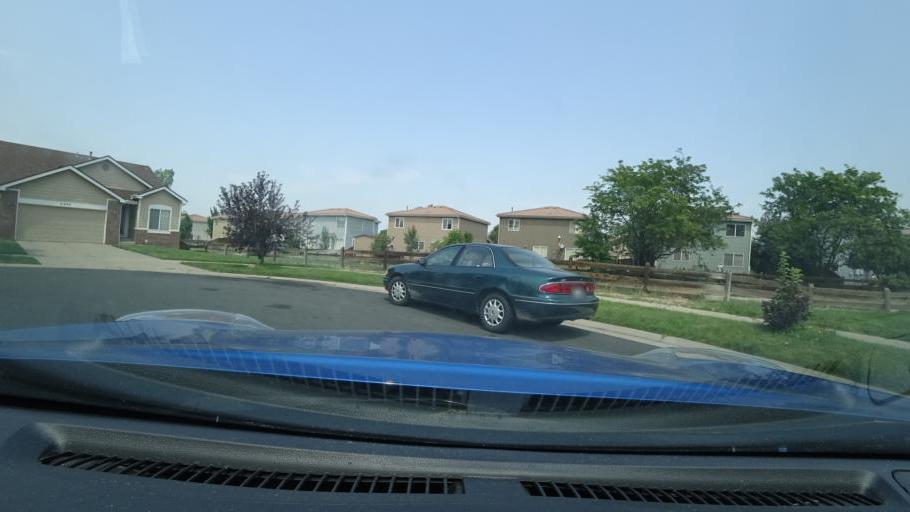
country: US
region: Colorado
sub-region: Adams County
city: Aurora
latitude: 39.7717
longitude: -104.7416
